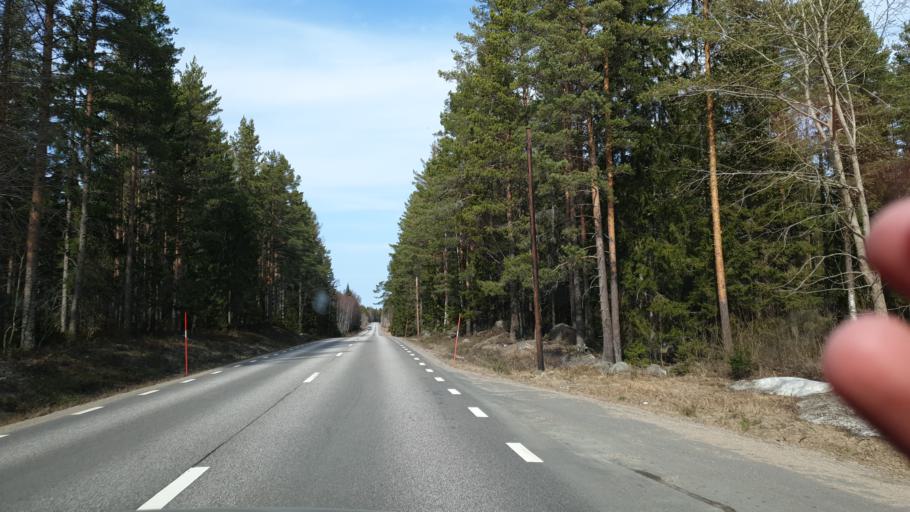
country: SE
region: Gaevleborg
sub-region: Gavle Kommun
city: Norrsundet
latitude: 61.0291
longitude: 17.1457
